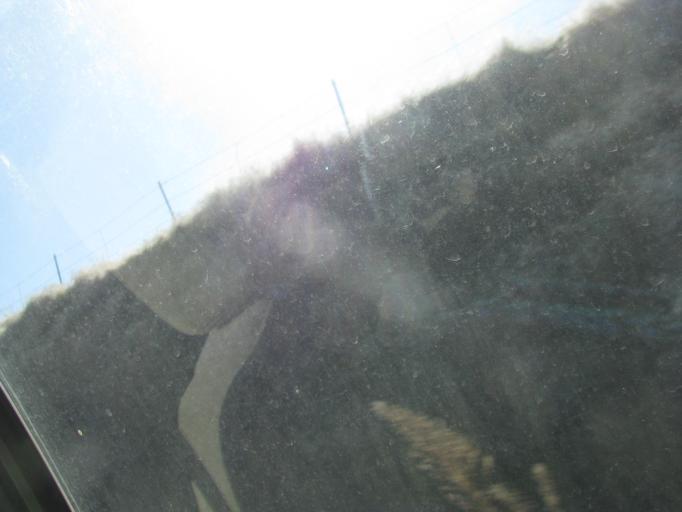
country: US
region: Washington
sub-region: Asotin County
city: Asotin
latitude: 46.3225
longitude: -117.0554
